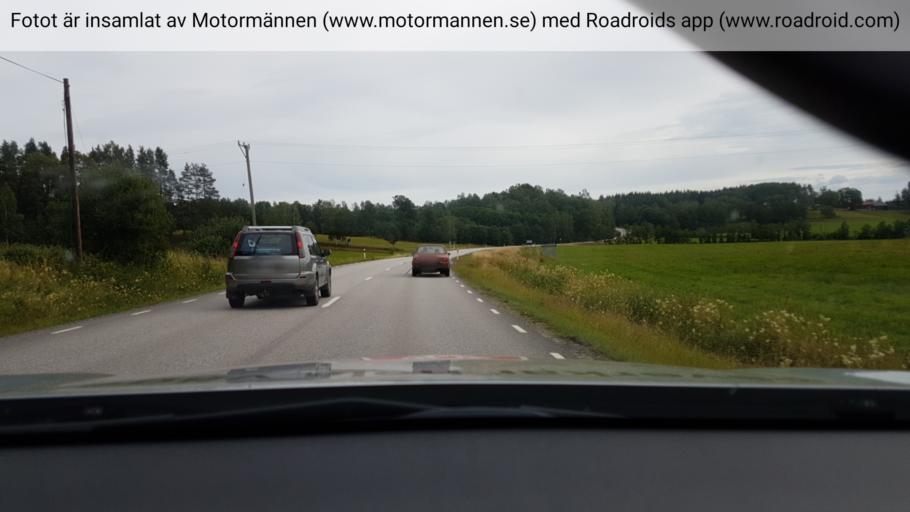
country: SE
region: Vaestra Goetaland
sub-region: Bengtsfors Kommun
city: Billingsfors
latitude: 58.9181
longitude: 12.2233
